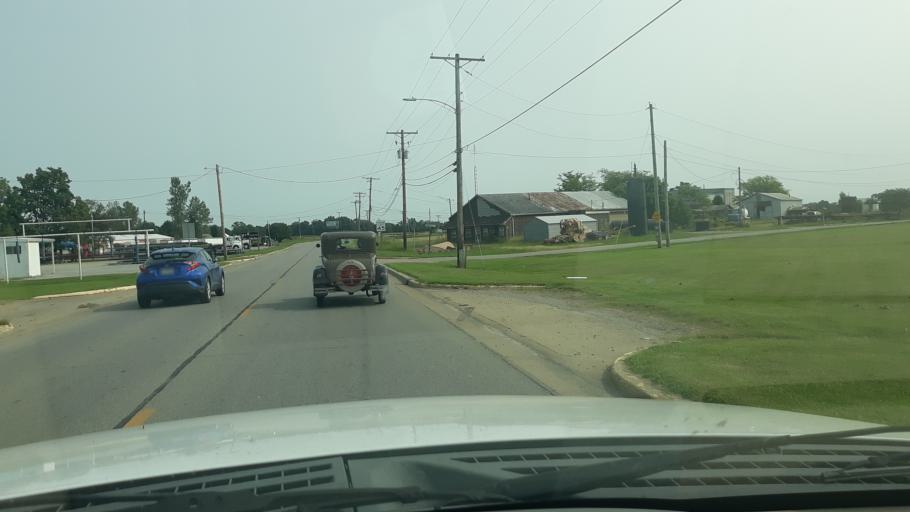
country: US
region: Illinois
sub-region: White County
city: Carmi
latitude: 38.0981
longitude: -88.1456
